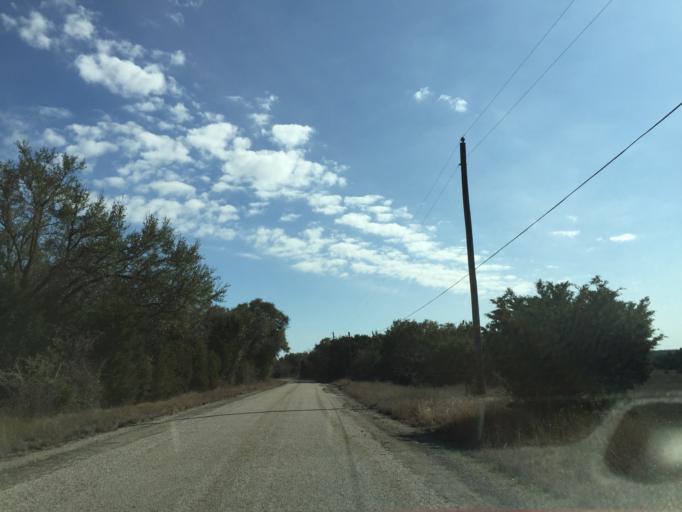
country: US
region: Texas
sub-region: Williamson County
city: Florence
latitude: 30.7759
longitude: -97.8905
